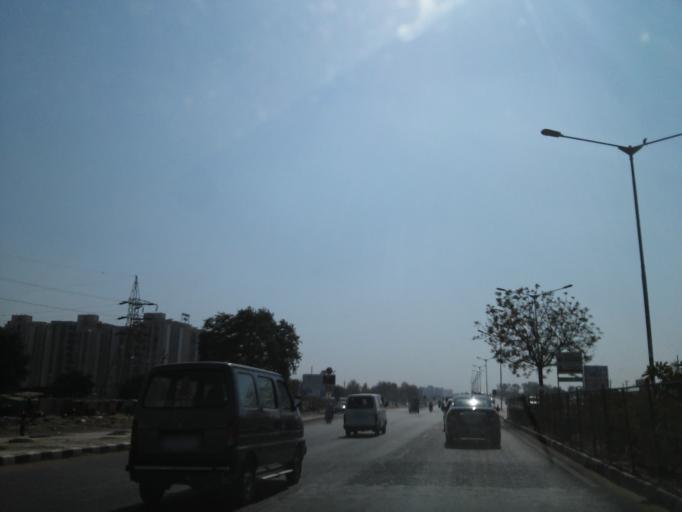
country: IN
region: Gujarat
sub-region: Gandhinagar
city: Adalaj
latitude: 23.1063
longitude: 72.5340
